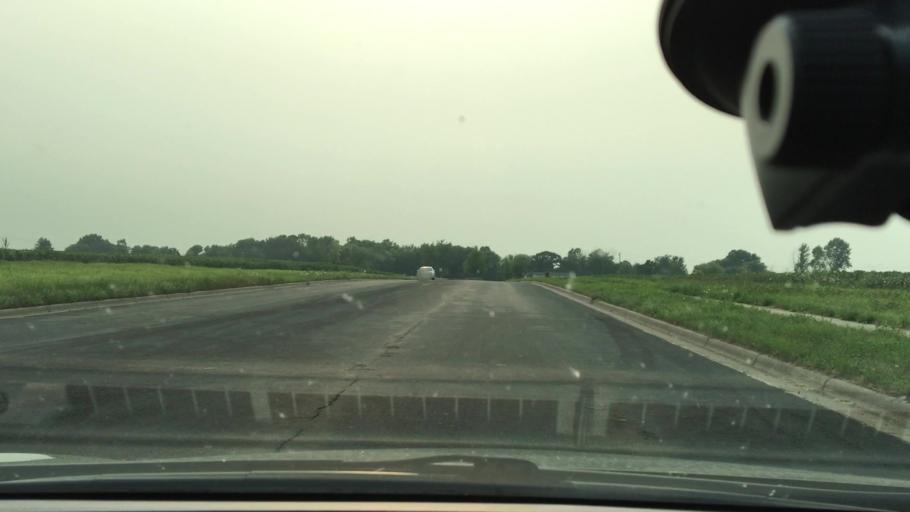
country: US
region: Minnesota
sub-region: Wright County
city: Albertville
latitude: 45.2562
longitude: -93.6599
